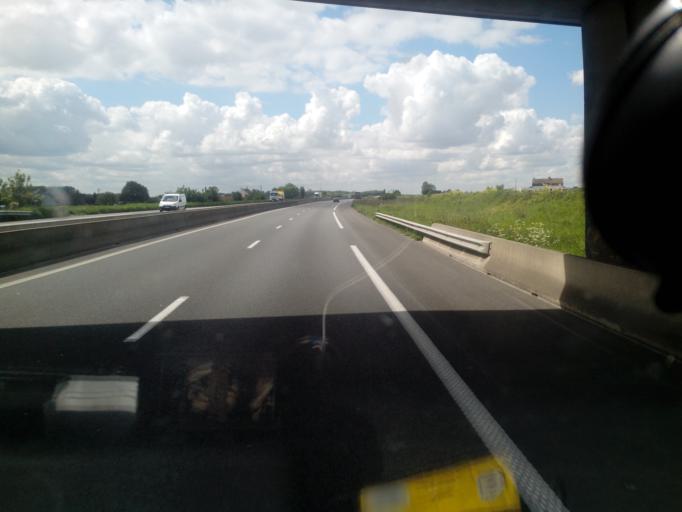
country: FR
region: Nord-Pas-de-Calais
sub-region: Departement du Nord
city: Godewaersvelde
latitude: 50.7540
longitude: 2.6548
